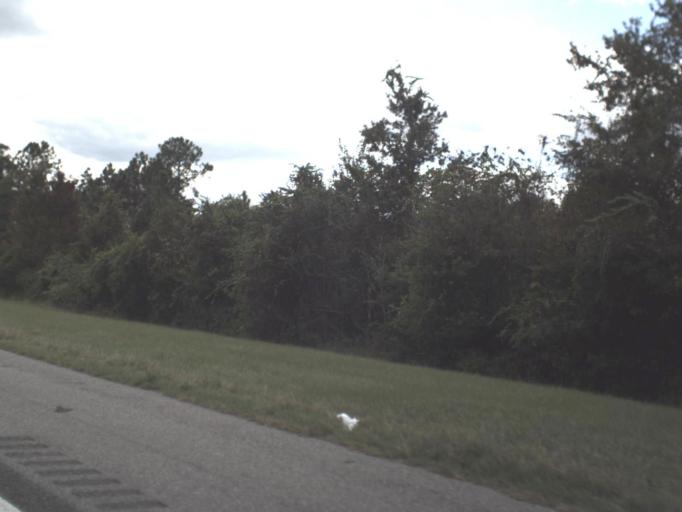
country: US
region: Florida
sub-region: Osceola County
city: Saint Cloud
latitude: 28.2279
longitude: -81.3224
